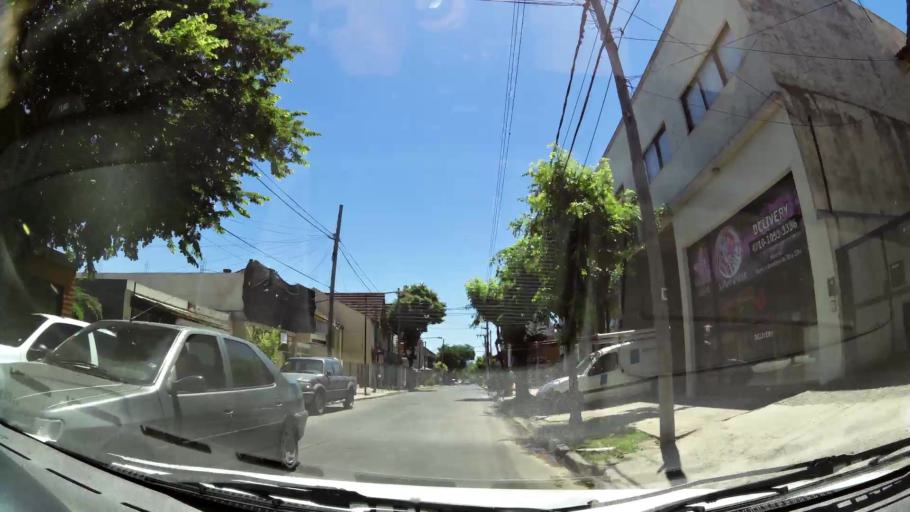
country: AR
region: Buenos Aires
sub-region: Partido de Tigre
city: Tigre
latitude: -34.4950
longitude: -58.5744
